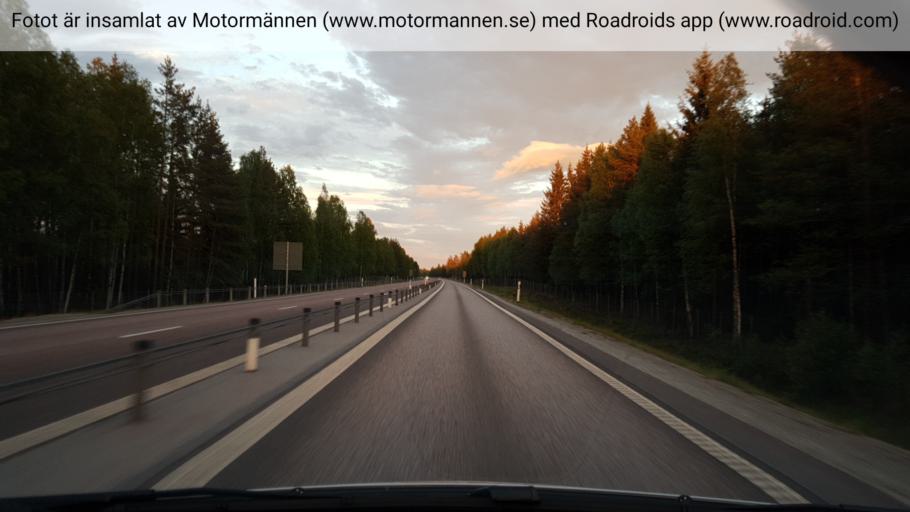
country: SE
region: Vaestmanland
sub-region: Surahammars Kommun
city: Ramnas
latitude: 59.8293
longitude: 16.0855
